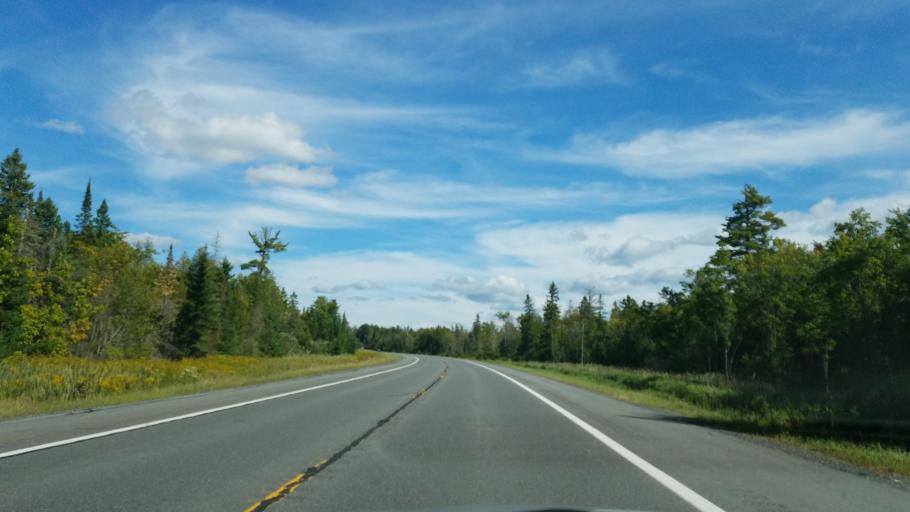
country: US
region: Michigan
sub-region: Baraga County
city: L'Anse
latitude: 46.5823
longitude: -88.4673
